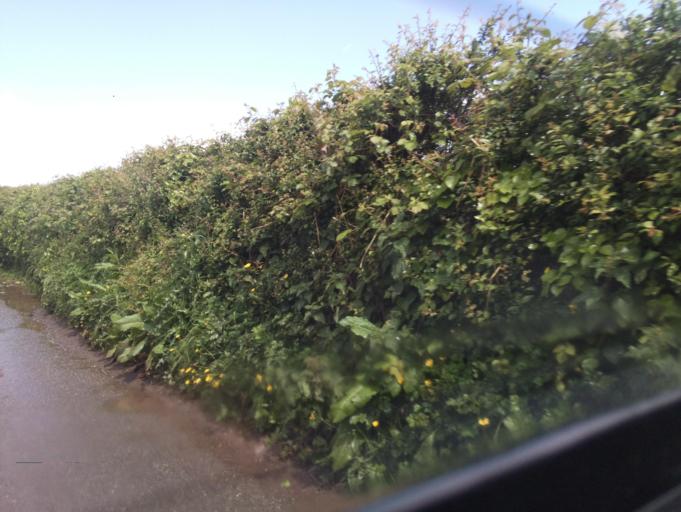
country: GB
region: England
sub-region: Devon
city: Dartmouth
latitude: 50.3559
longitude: -3.5412
